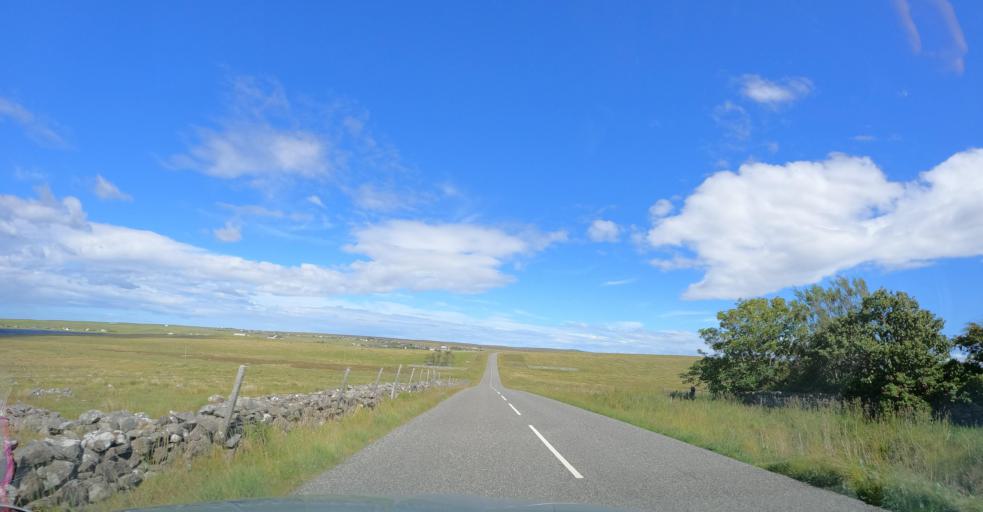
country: GB
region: Scotland
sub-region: Eilean Siar
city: Isle of Lewis
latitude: 58.3483
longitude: -6.5406
